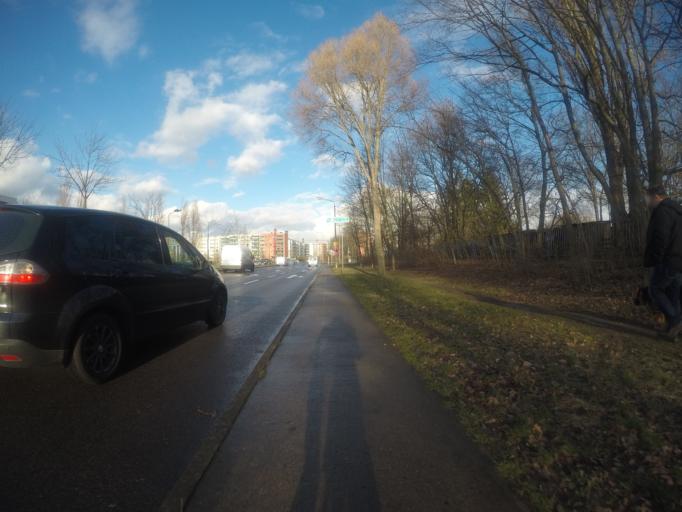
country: DE
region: Berlin
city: Kaulsdorf
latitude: 52.5168
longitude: 13.5880
